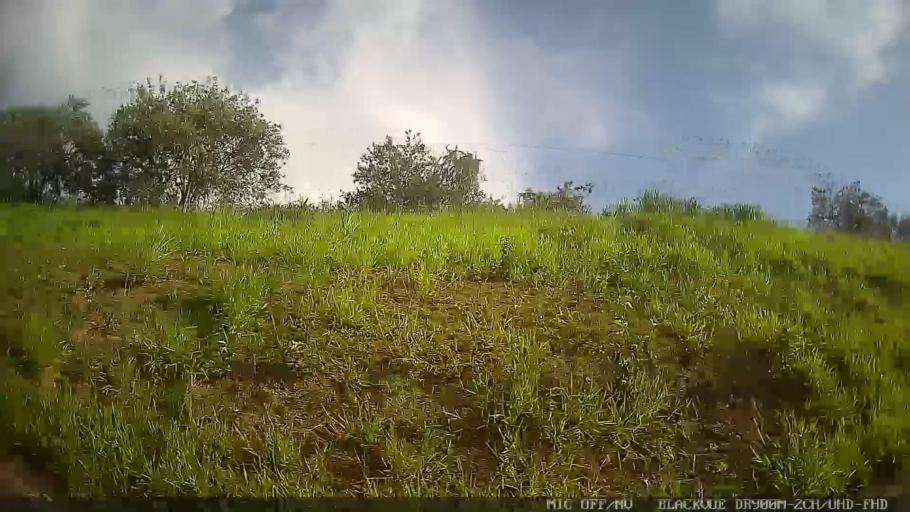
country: BR
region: Sao Paulo
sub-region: Tiete
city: Tiete
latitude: -23.0863
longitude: -47.6777
